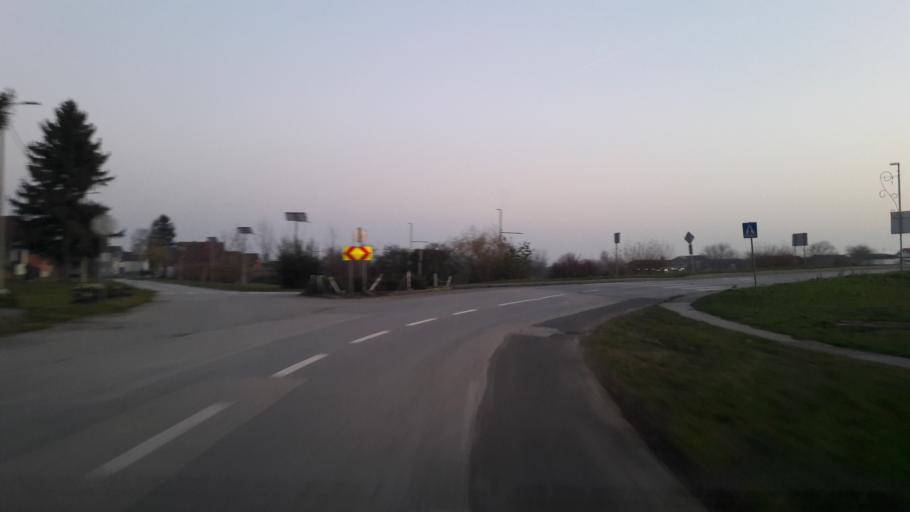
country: HR
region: Vukovarsko-Srijemska
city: Nijemci
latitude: 45.1427
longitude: 19.0373
